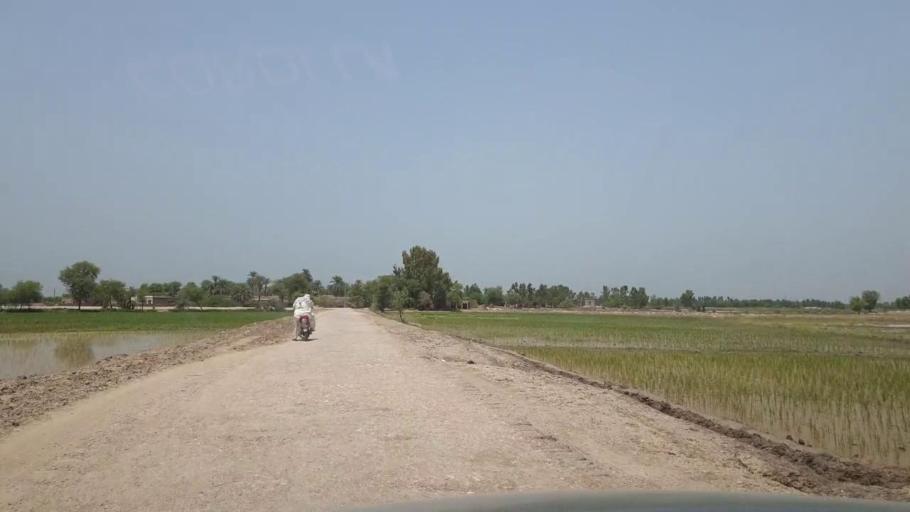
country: PK
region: Sindh
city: Garhi Yasin
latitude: 27.8683
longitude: 68.4561
